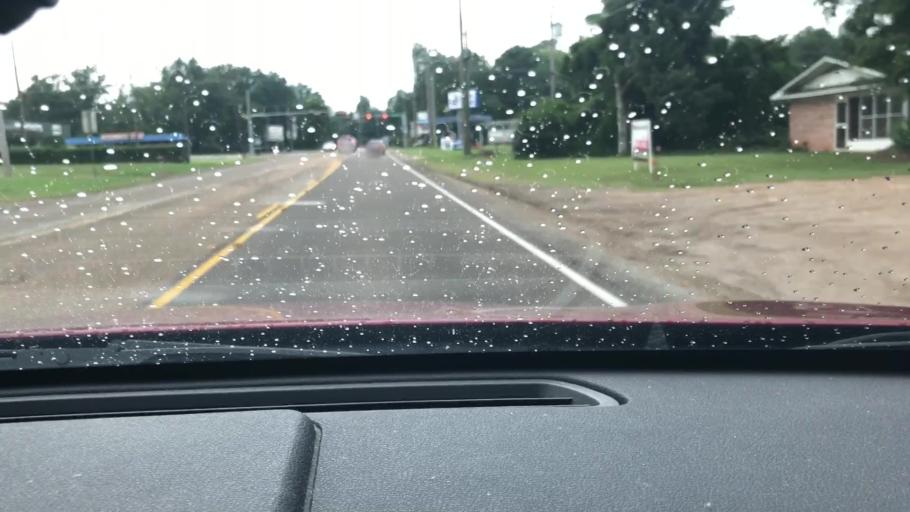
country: US
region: Texas
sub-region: Bowie County
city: Nash
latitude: 33.4425
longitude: -94.1294
